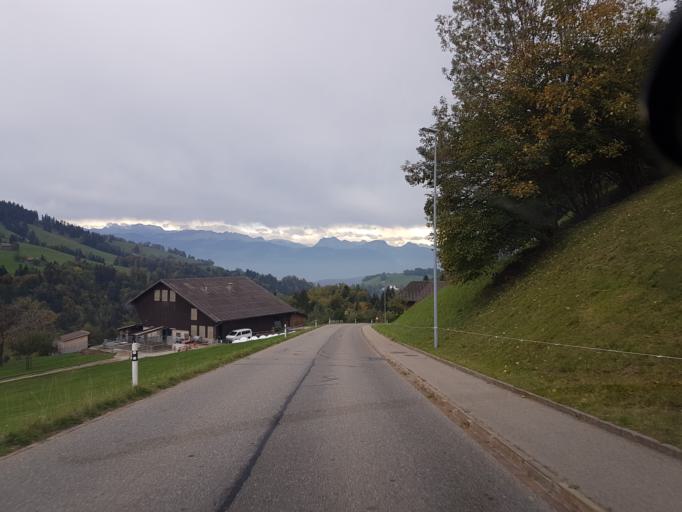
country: CH
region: Saint Gallen
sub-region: Wahlkreis See-Gaster
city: Goldingen
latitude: 47.2800
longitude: 8.9794
